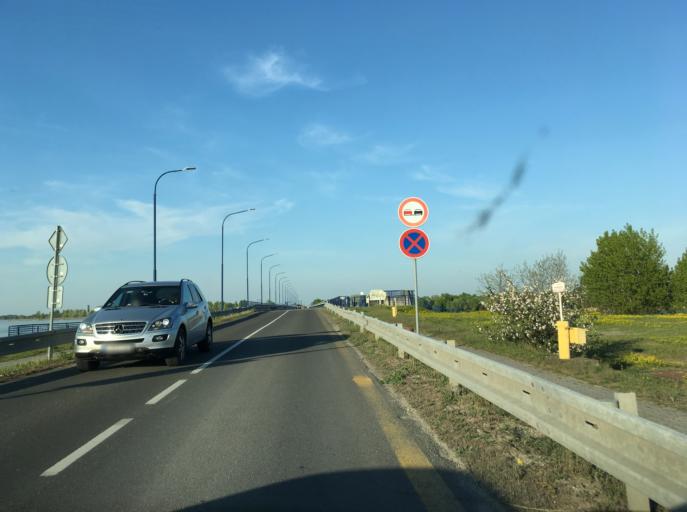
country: HU
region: Gyor-Moson-Sopron
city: Rajka
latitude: 48.0253
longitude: 17.2174
